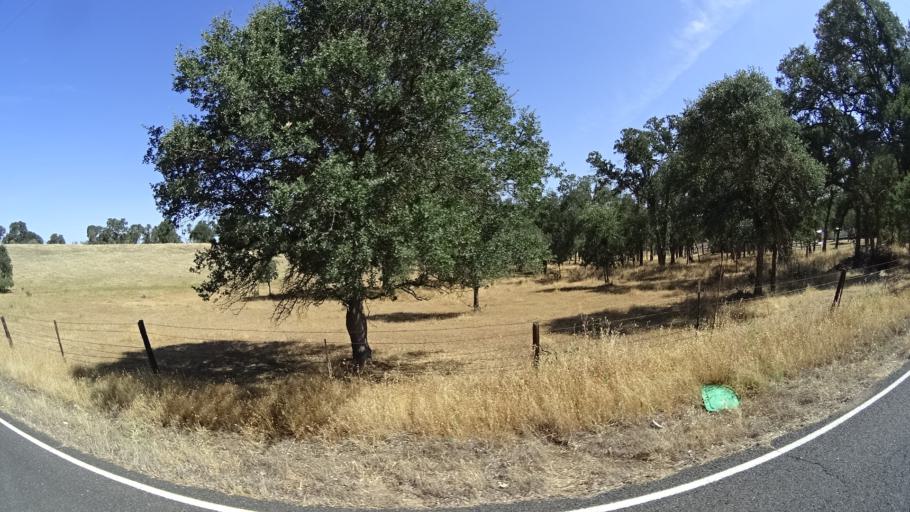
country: US
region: California
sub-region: Calaveras County
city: Rancho Calaveras
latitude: 38.1340
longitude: -120.9105
